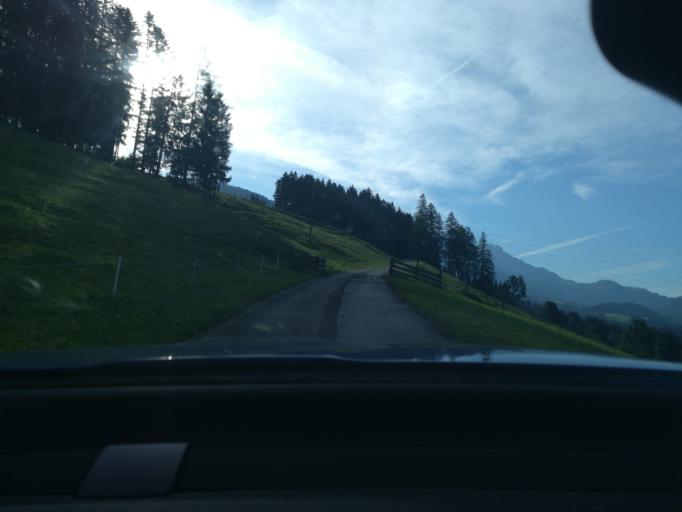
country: AT
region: Salzburg
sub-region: Politischer Bezirk Hallein
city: Abtenau
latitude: 47.5637
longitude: 13.4016
